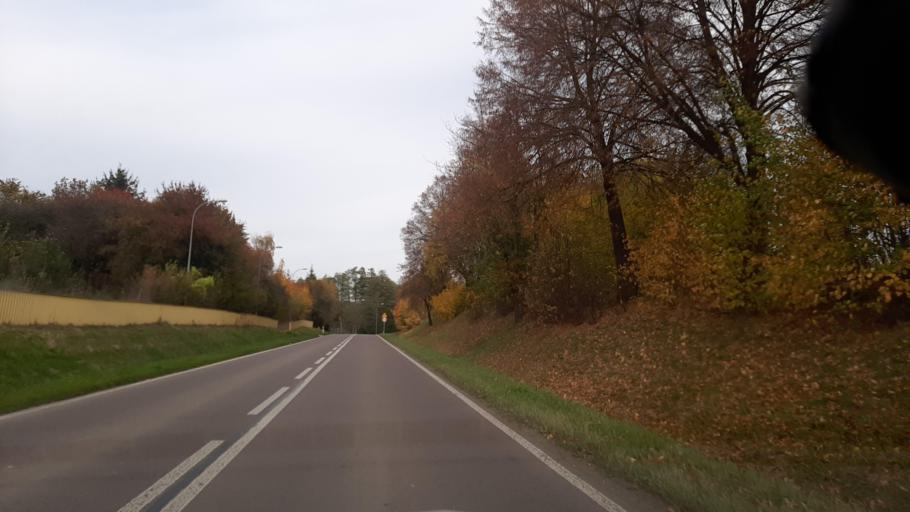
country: PL
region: Lublin Voivodeship
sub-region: Powiat pulawski
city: Naleczow
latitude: 51.3145
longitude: 22.2211
